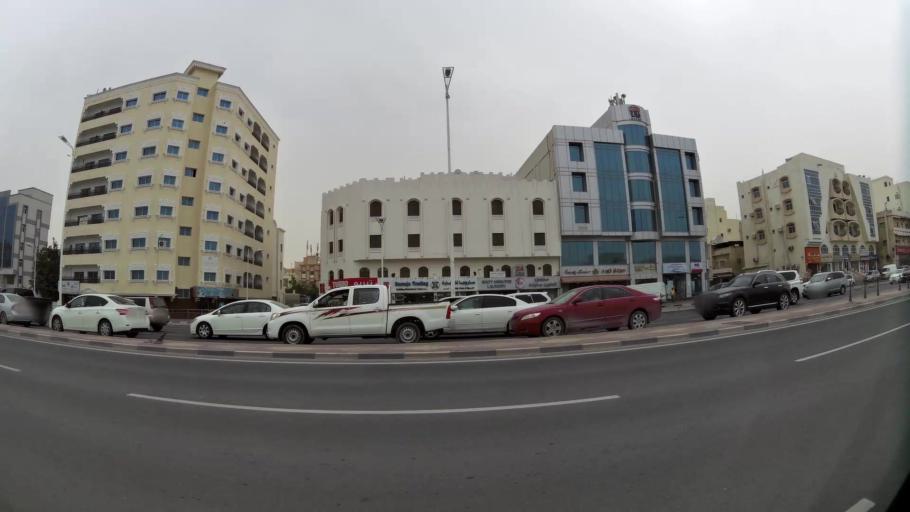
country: QA
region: Baladiyat ad Dawhah
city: Doha
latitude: 25.3011
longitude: 51.5017
